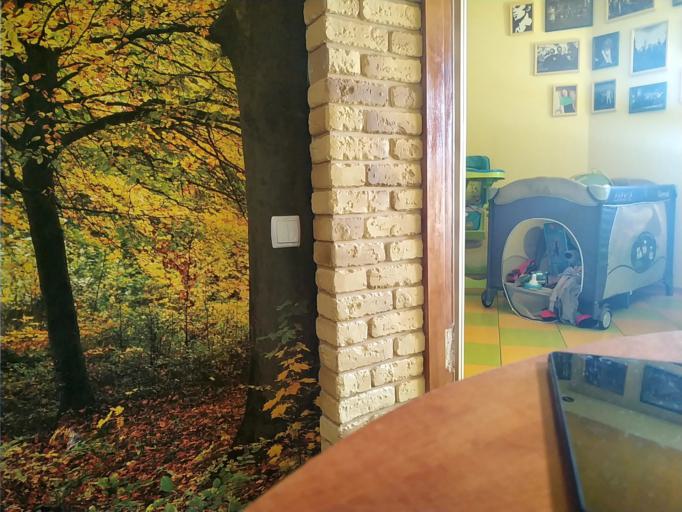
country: RU
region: Tverskaya
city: Vyshniy Volochek
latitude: 57.5942
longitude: 34.5297
